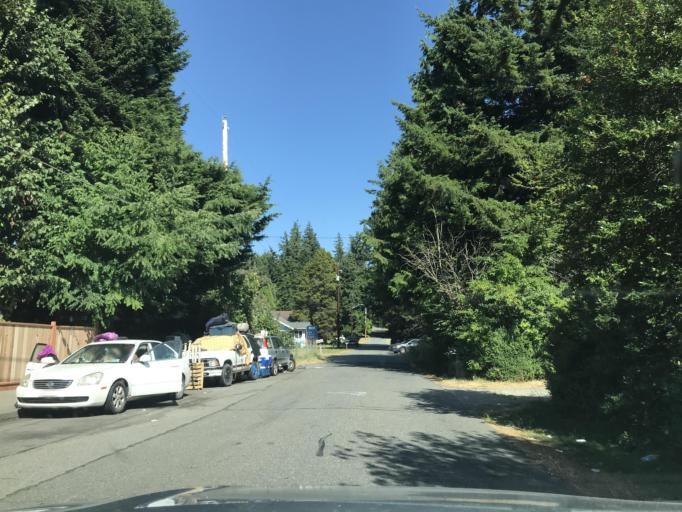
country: US
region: Washington
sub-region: Whatcom County
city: Bellingham
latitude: 48.7807
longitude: -122.4851
